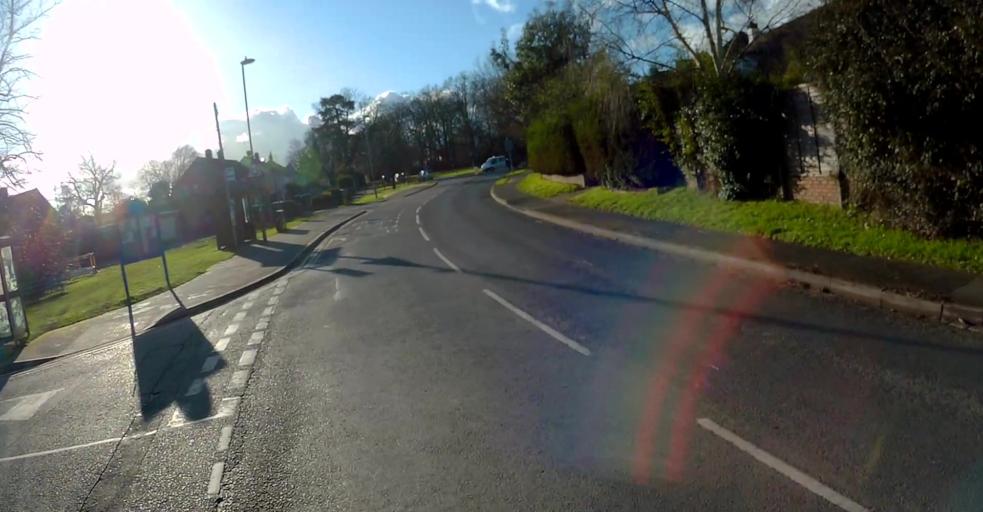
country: GB
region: England
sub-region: Surrey
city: Addlestone
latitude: 51.3629
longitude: -0.5074
